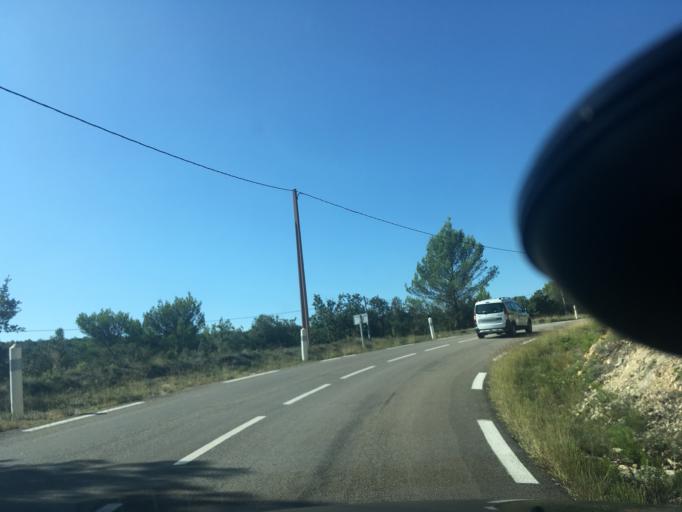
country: FR
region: Provence-Alpes-Cote d'Azur
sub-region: Departement du Var
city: Barjols
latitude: 43.6043
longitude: 6.0694
